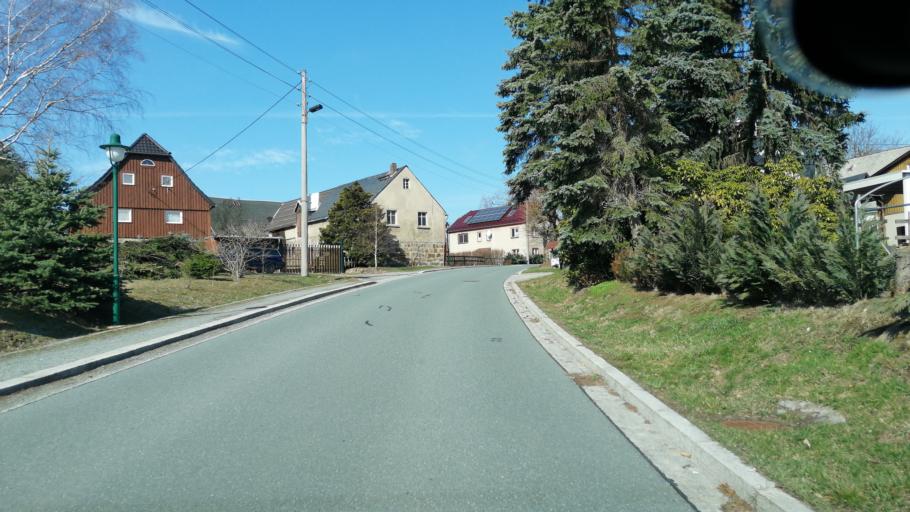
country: DE
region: Saxony
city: Schonbach
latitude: 51.0677
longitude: 14.5543
